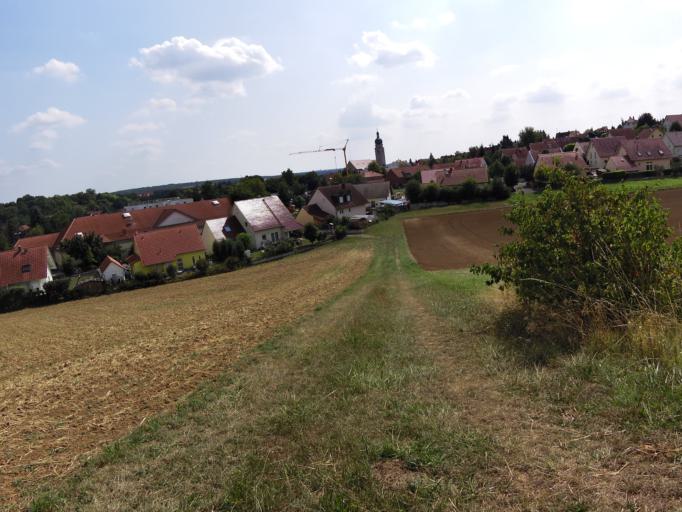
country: DE
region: Bavaria
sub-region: Regierungsbezirk Unterfranken
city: Estenfeld
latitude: 49.8340
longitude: 10.0060
